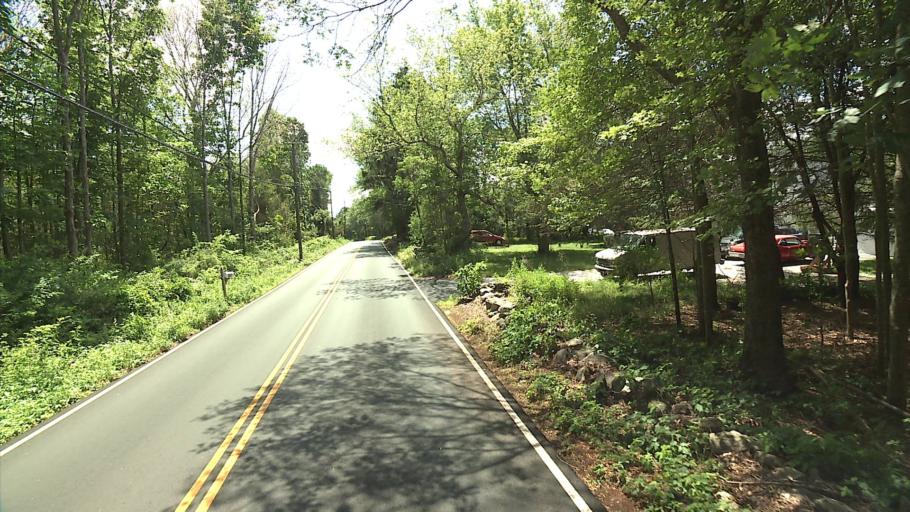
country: US
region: Connecticut
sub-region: New London County
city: Preston City
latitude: 41.5719
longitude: -71.8934
